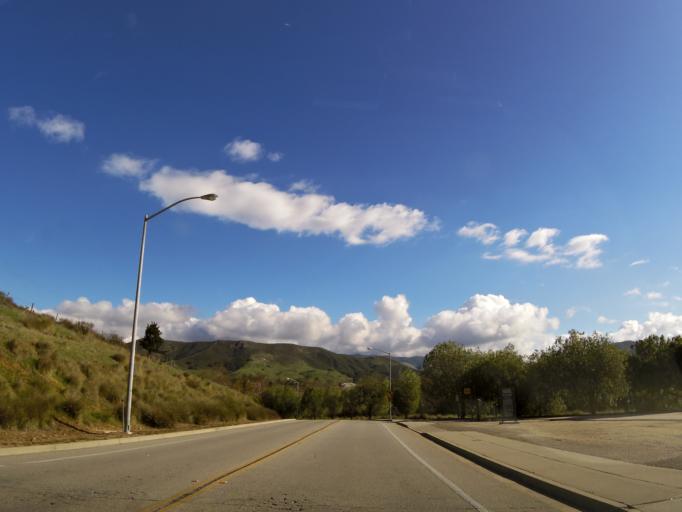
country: US
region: California
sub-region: San Luis Obispo County
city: San Luis Obispo
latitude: 35.2989
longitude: -120.6725
